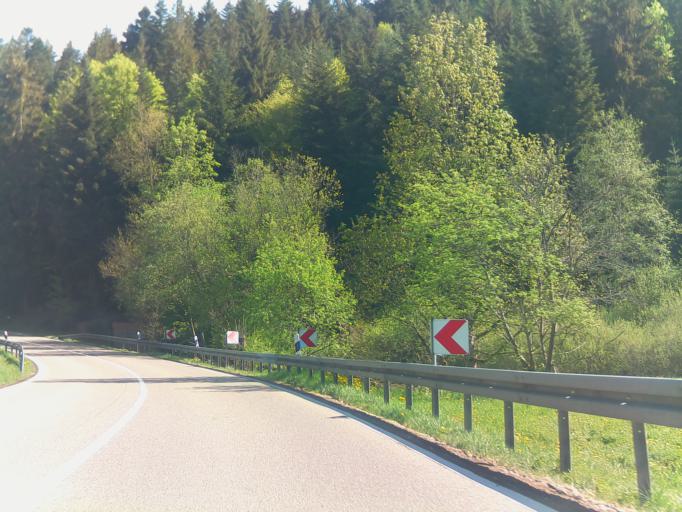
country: DE
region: Baden-Wuerttemberg
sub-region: Karlsruhe Region
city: Bad Wildbad
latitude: 48.7268
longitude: 8.5712
